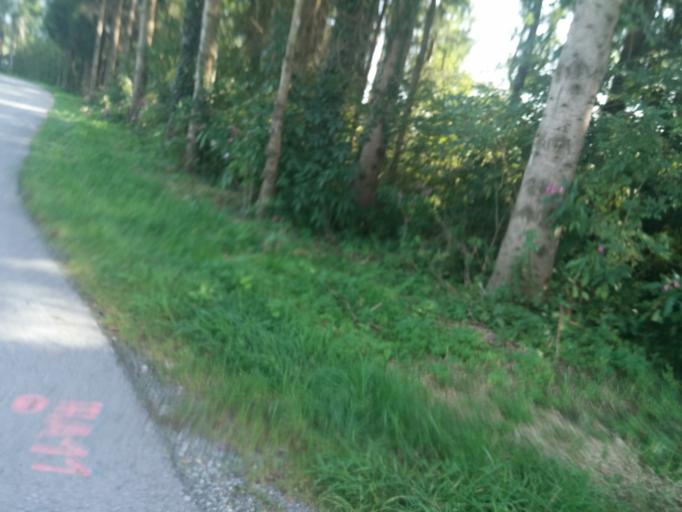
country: DE
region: Bavaria
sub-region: Upper Bavaria
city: Oberaudorf
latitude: 47.6545
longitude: 12.1809
